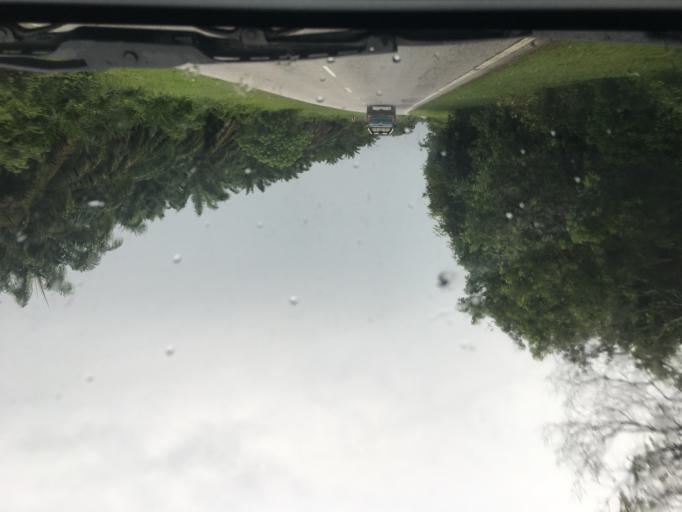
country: MY
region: Kedah
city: Sungai Petani
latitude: 5.6307
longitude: 100.6320
